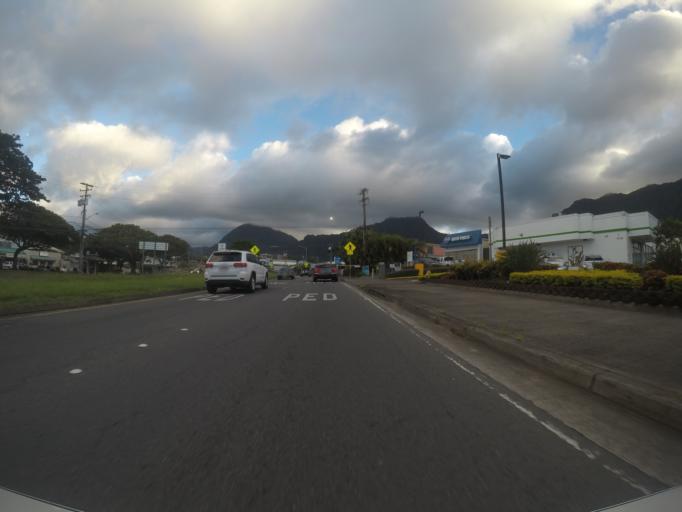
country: US
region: Hawaii
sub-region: Honolulu County
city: Kane'ohe
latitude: 21.4022
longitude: -157.7999
